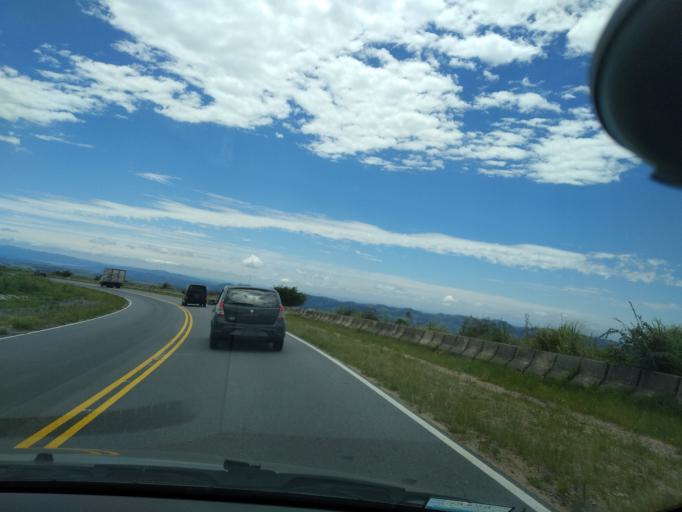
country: AR
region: Cordoba
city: Cuesta Blanca
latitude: -31.6379
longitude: -64.6772
